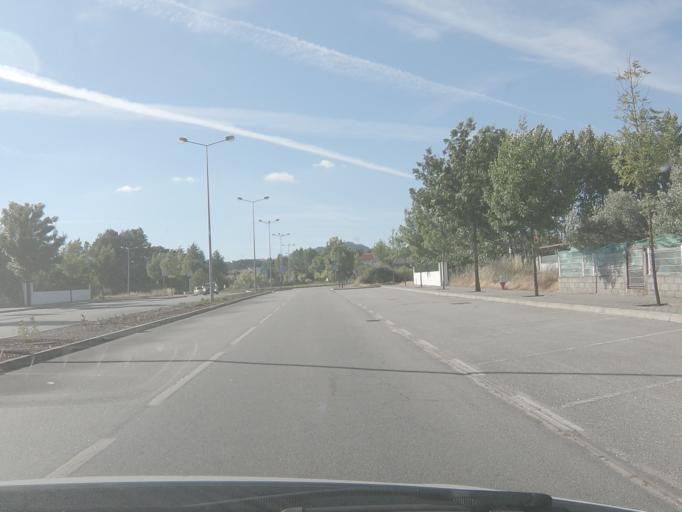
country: PT
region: Viseu
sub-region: Viseu
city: Viseu
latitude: 40.6709
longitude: -7.9047
